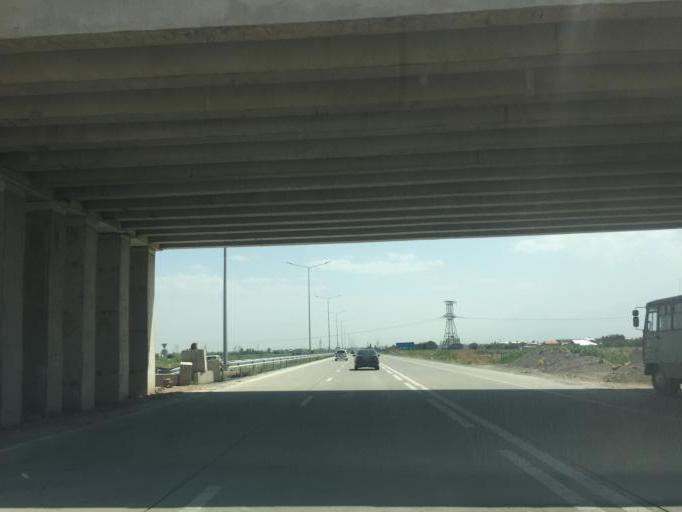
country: AM
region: Ararat
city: Masis
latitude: 40.0802
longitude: 44.4530
